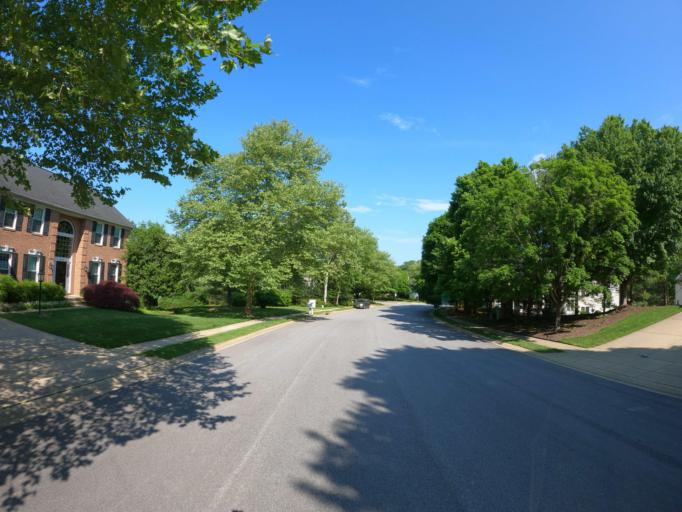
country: US
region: Maryland
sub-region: Howard County
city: Riverside
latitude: 39.1966
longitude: -76.9128
